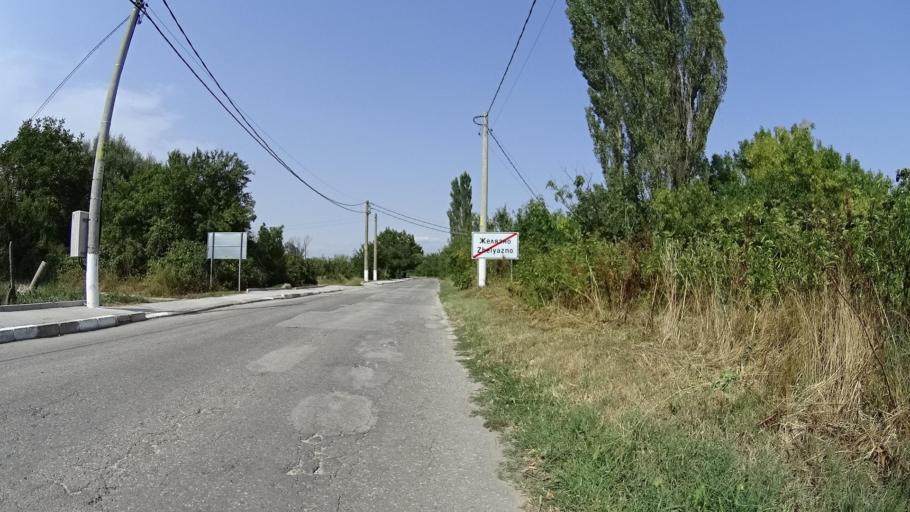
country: BG
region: Plovdiv
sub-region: Obshtina Plovdiv
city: Plovdiv
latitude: 42.2189
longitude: 24.7841
